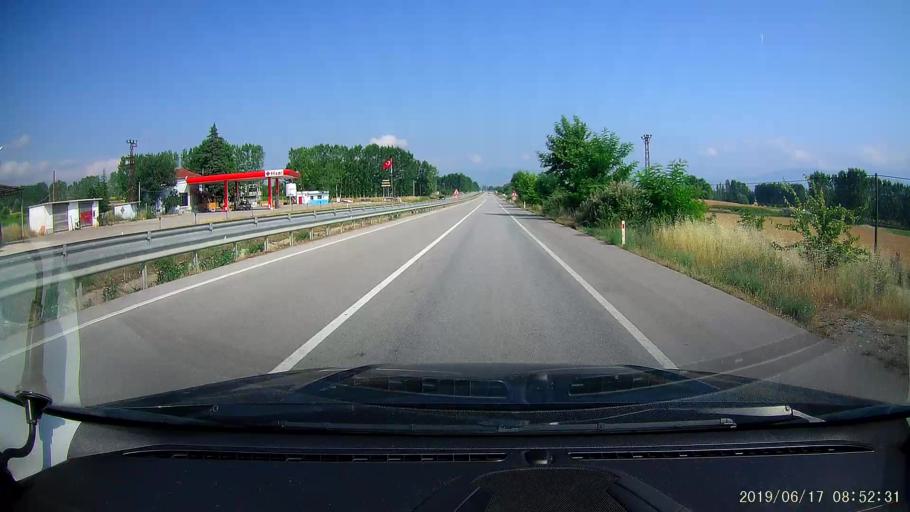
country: TR
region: Tokat
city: Erbaa
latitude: 40.6988
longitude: 36.4954
